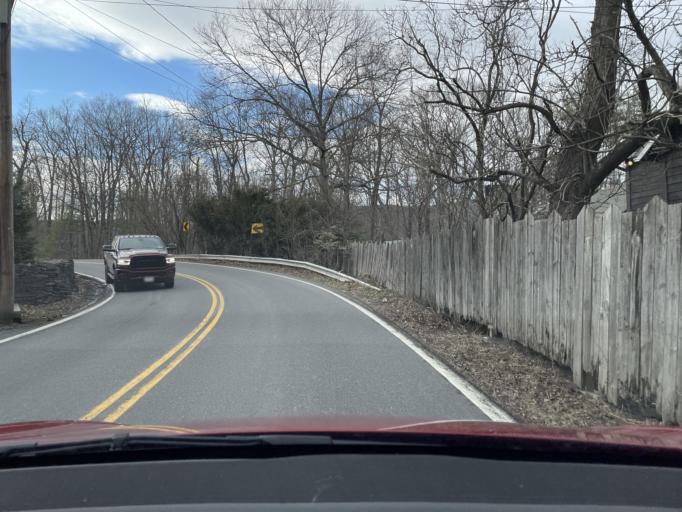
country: US
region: New York
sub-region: Ulster County
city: Zena
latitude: 42.0337
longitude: -74.0839
